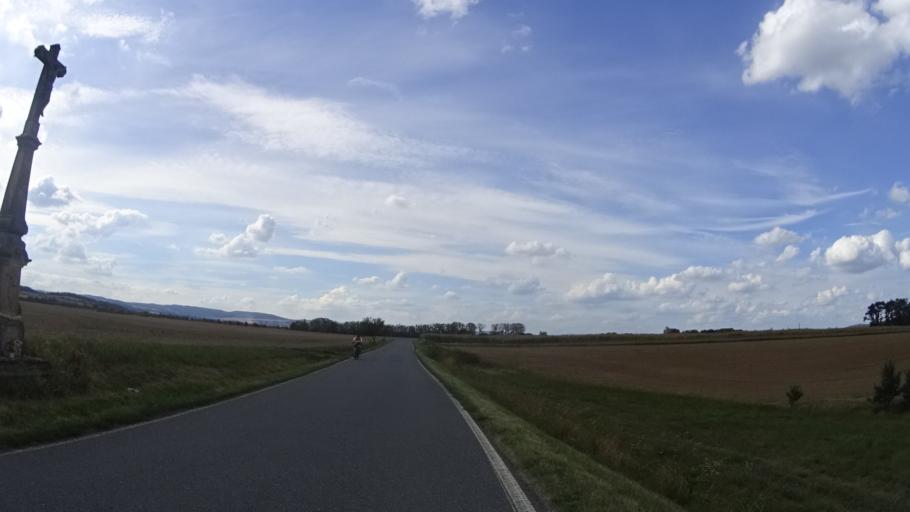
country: CZ
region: Olomoucky
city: Bila Lhota
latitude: 49.7351
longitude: 16.9761
